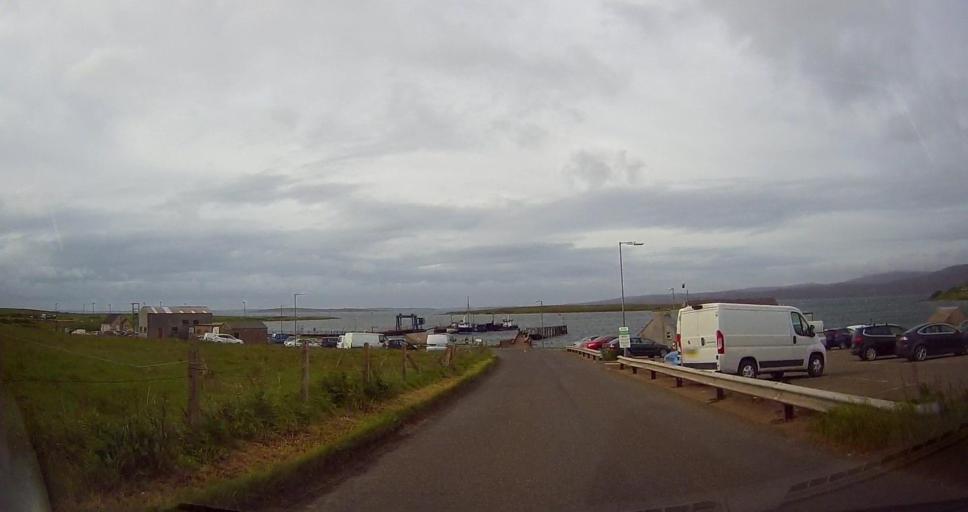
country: GB
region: Scotland
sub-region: Orkney Islands
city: Stromness
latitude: 58.9191
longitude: -3.1845
